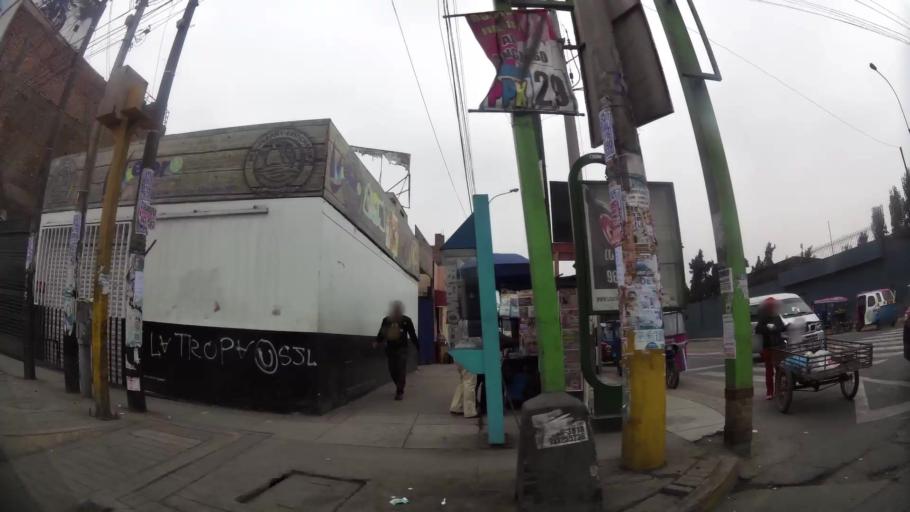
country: PE
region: Lima
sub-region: Lima
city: La Molina
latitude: -12.0531
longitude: -76.9613
